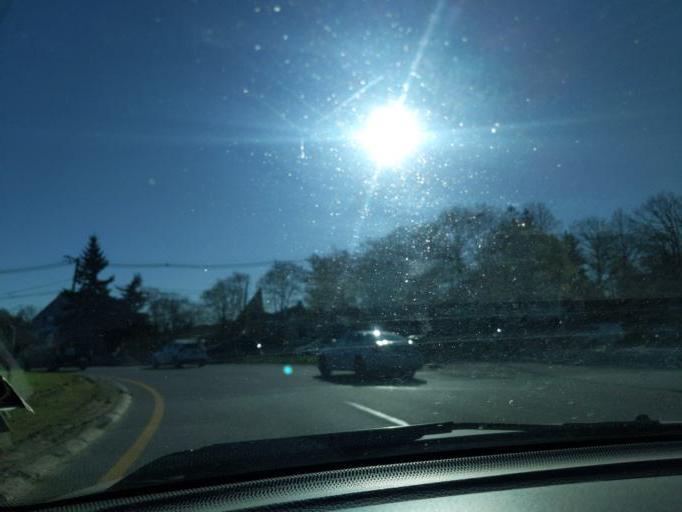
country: US
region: Massachusetts
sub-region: Essex County
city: Gloucester
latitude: 42.6216
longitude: -70.6761
